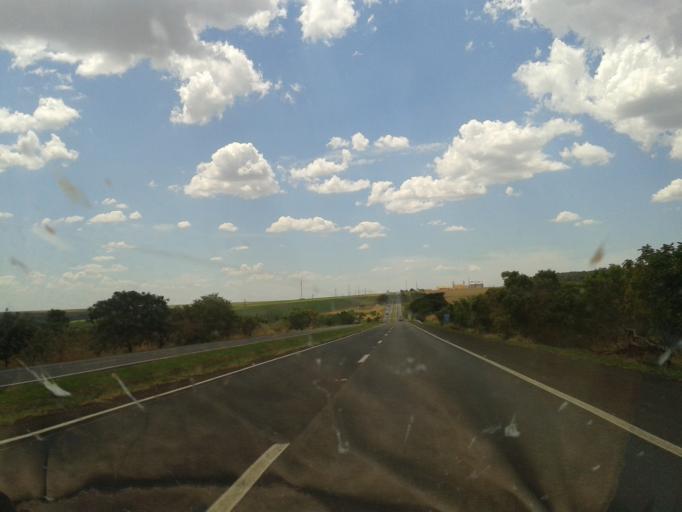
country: BR
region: Minas Gerais
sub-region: Uberlandia
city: Uberlandia
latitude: -19.0957
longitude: -48.1827
